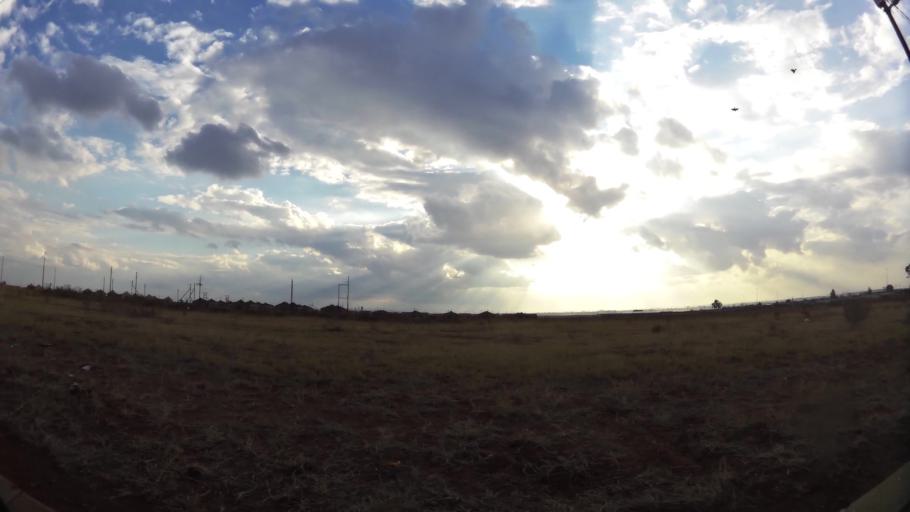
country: ZA
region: Gauteng
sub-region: Sedibeng District Municipality
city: Vanderbijlpark
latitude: -26.6085
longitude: 27.8111
